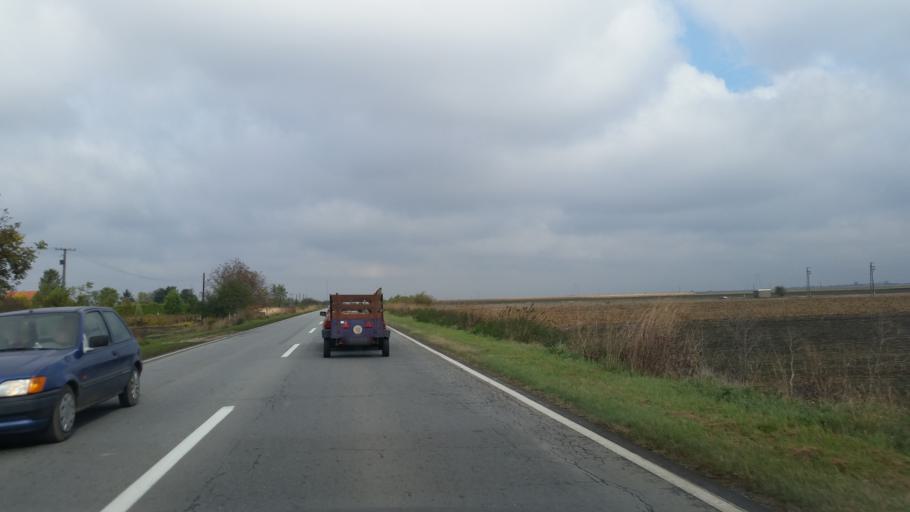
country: RS
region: Autonomna Pokrajina Vojvodina
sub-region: Srednjebanatski Okrug
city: Zrenjanin
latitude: 45.4213
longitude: 20.3713
